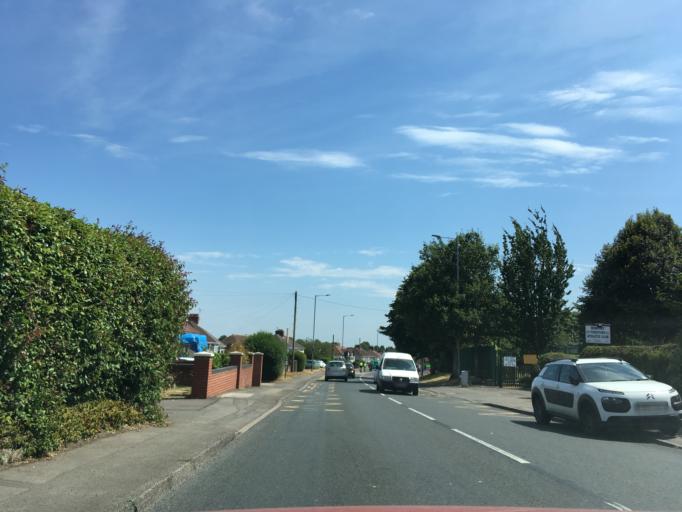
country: GB
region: Wales
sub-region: Newport
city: Newport
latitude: 51.5876
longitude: -3.0388
